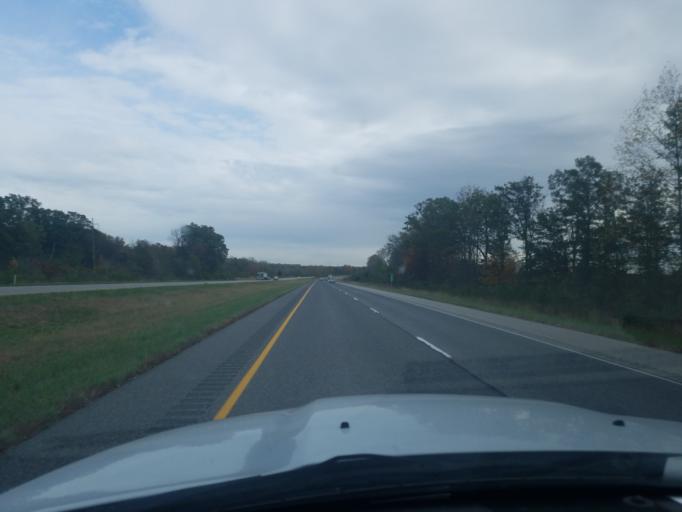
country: US
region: Indiana
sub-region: Warrick County
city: Boonville
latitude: 38.2007
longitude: -87.2476
